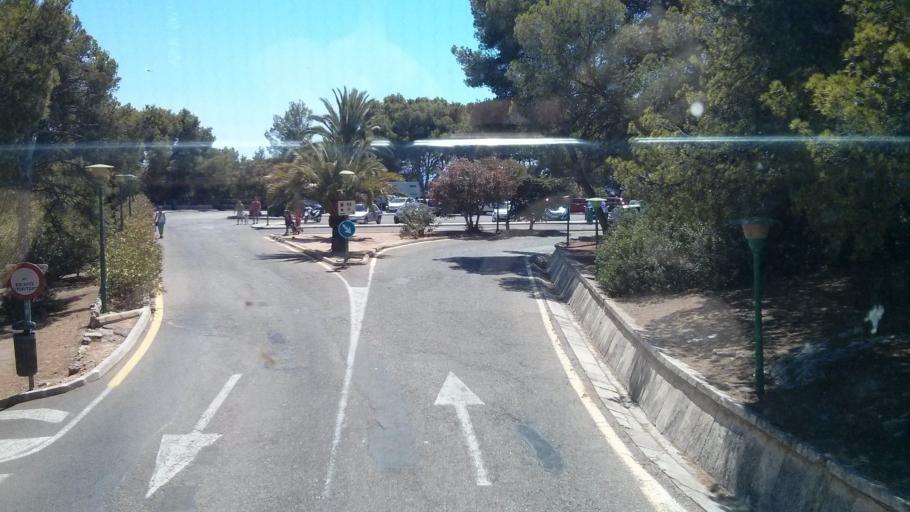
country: ES
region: Balearic Islands
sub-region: Illes Balears
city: Palma
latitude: 39.5632
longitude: 2.6199
